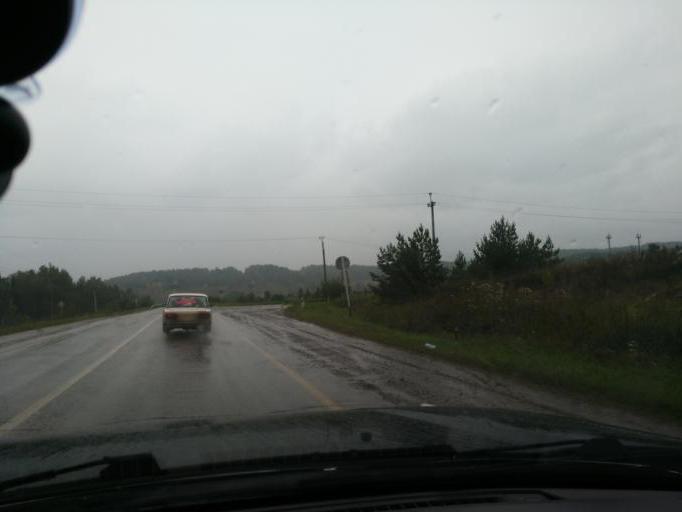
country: RU
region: Perm
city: Osa
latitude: 57.1948
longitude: 55.5917
